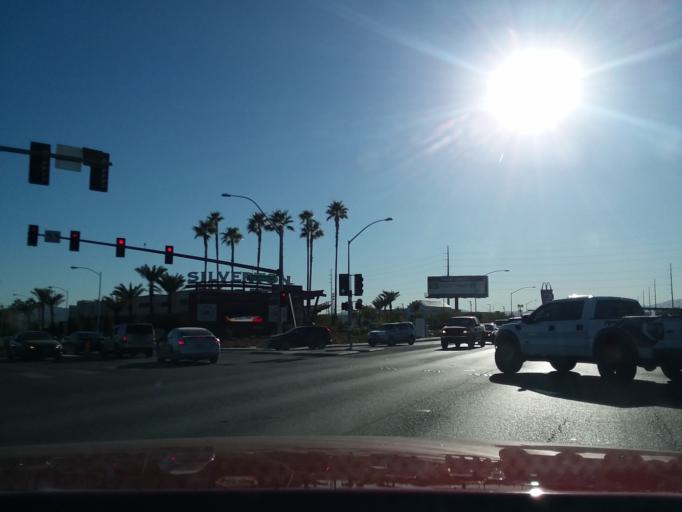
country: US
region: Nevada
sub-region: Clark County
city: Enterprise
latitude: 36.0414
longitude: -115.1880
